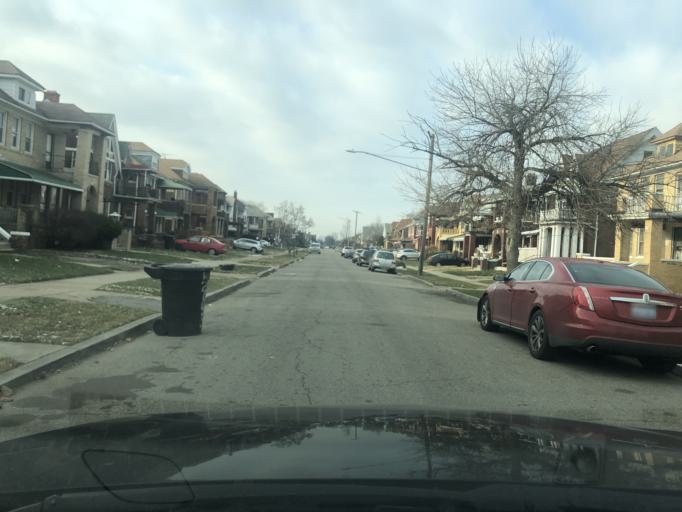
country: US
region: Michigan
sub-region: Wayne County
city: Highland Park
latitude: 42.3951
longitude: -83.1243
